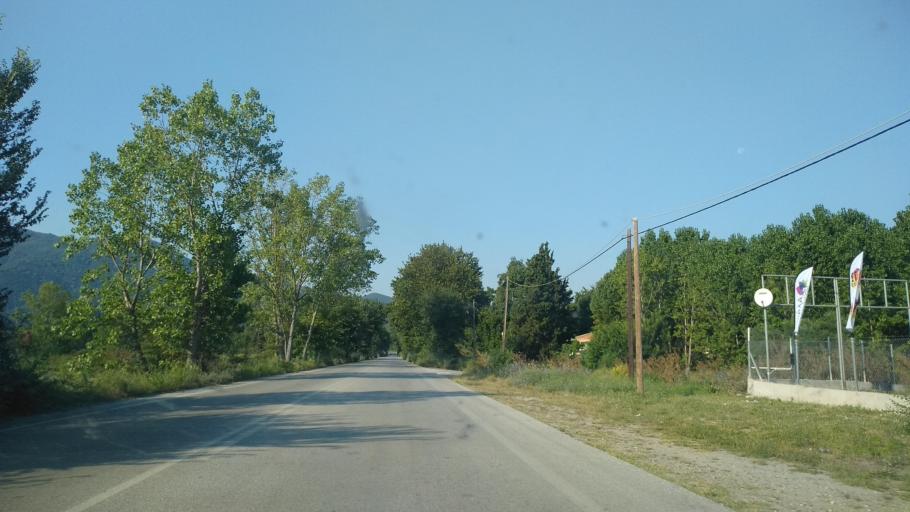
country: GR
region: Central Macedonia
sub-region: Nomos Thessalonikis
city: Nea Vrasna
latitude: 40.6865
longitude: 23.6788
